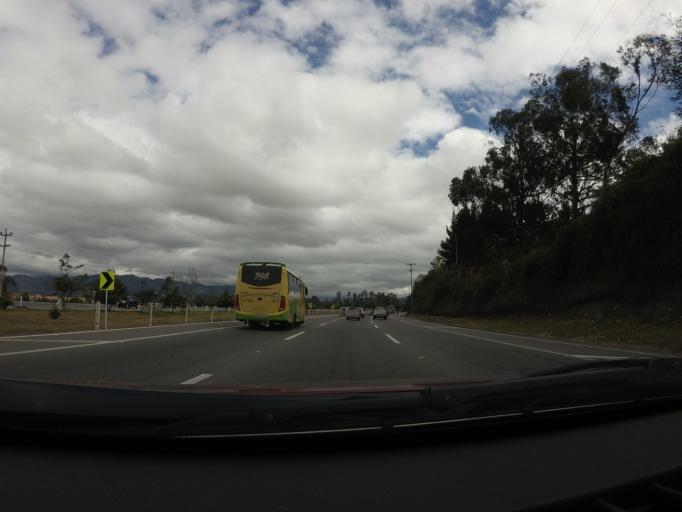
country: CO
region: Cundinamarca
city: Chia
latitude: 4.8658
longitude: -74.0242
